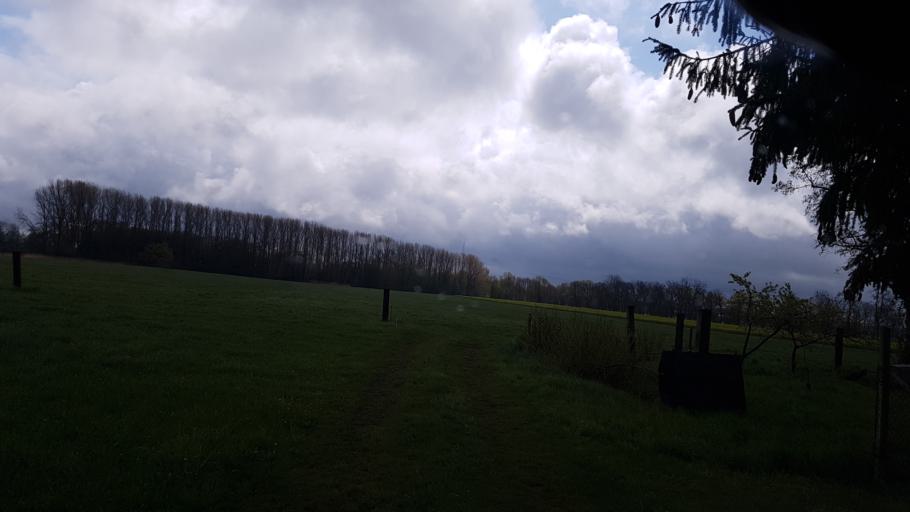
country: DE
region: Brandenburg
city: Doberlug-Kirchhain
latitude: 51.6512
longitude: 13.5511
